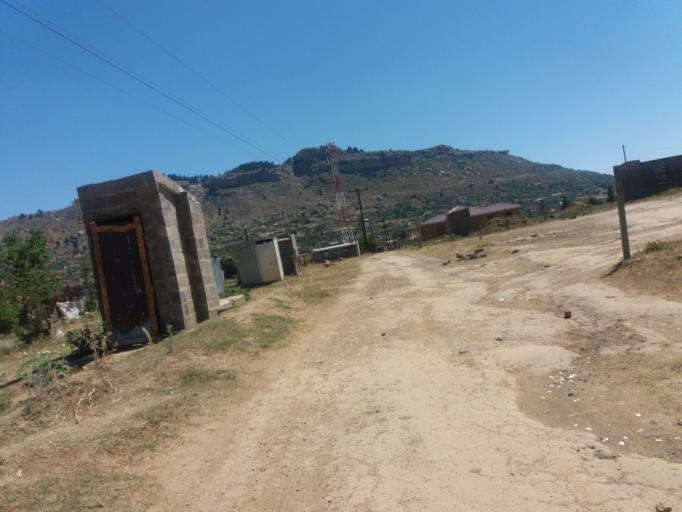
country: LS
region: Maseru
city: Maseru
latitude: -29.3663
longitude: 27.4726
